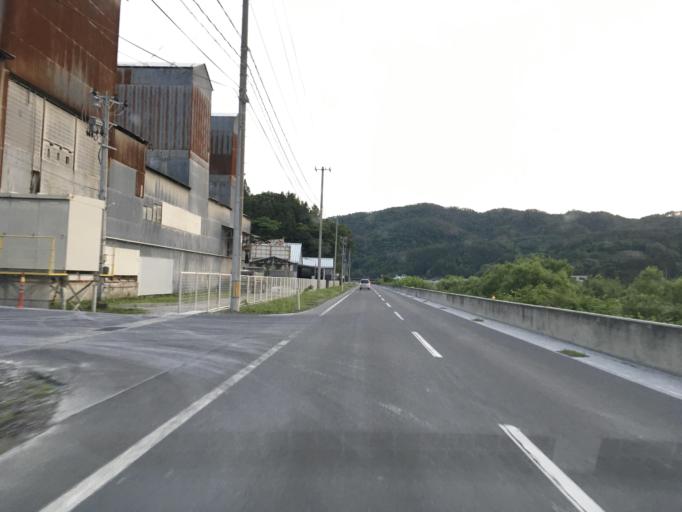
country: JP
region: Iwate
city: Ichinoseki
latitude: 38.9824
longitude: 141.2476
